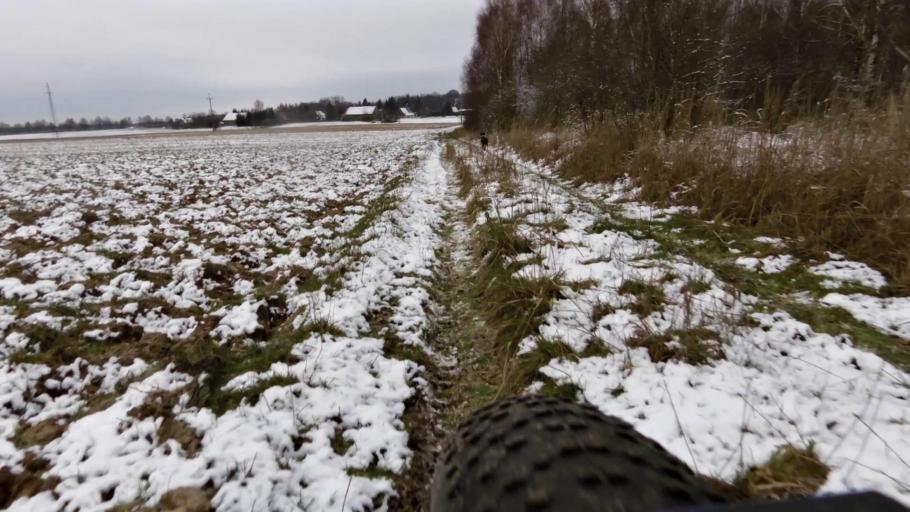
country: PL
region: West Pomeranian Voivodeship
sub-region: Powiat walecki
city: Miroslawiec
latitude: 53.3448
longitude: 16.2687
